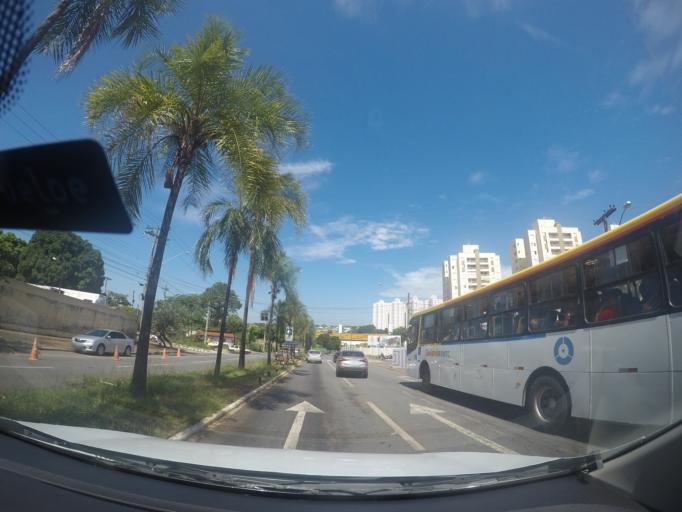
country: BR
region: Goias
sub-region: Goiania
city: Goiania
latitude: -16.7123
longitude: -49.3167
